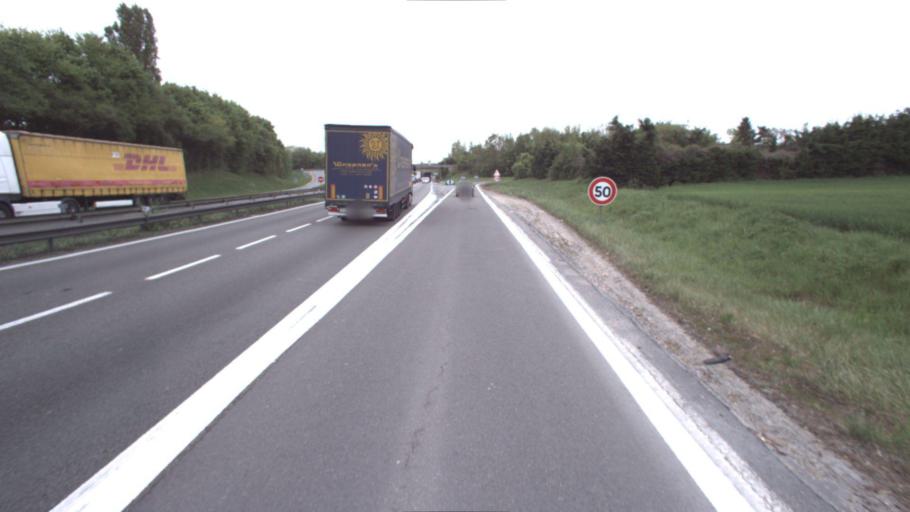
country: FR
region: Ile-de-France
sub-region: Departement de Seine-et-Marne
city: Servon
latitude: 48.7153
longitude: 2.5998
